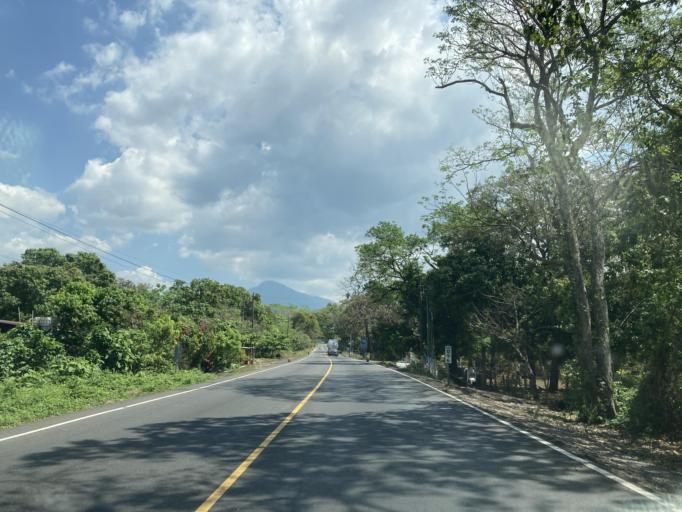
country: GT
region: Santa Rosa
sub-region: Municipio de Taxisco
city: Taxisco
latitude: 14.0950
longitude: -90.5467
